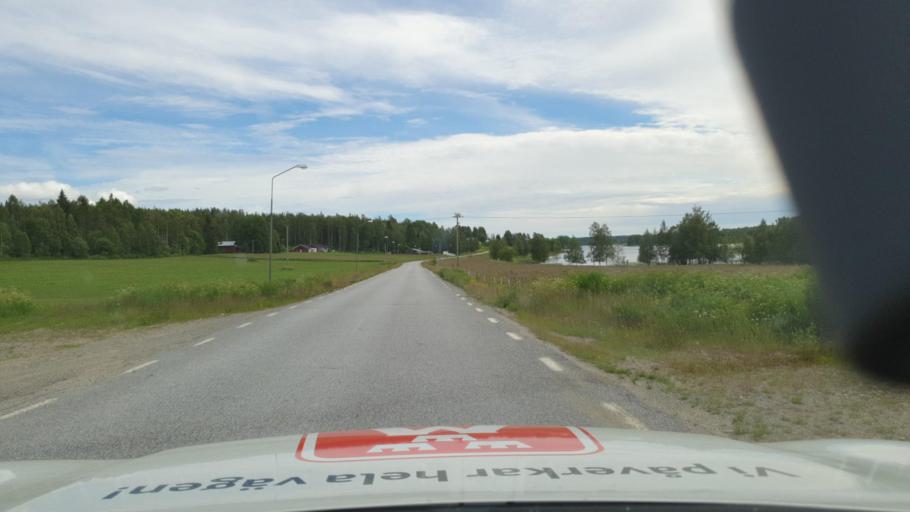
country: SE
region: Vaesterbotten
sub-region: Skelleftea Kommun
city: Burea
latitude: 64.5010
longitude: 21.0150
